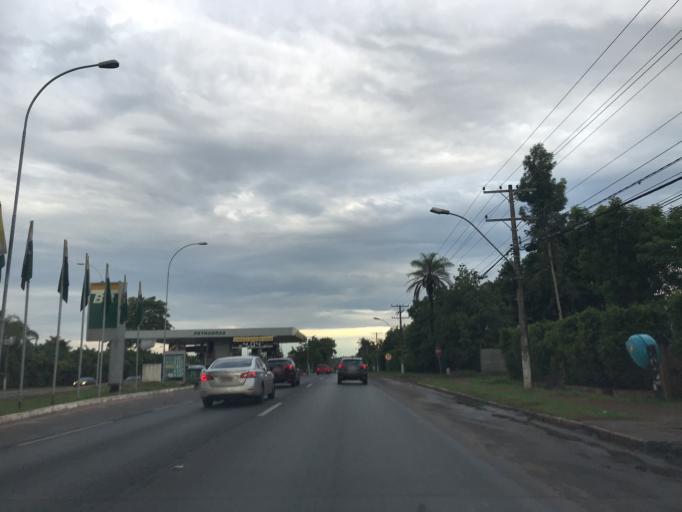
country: BR
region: Federal District
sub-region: Brasilia
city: Brasilia
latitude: -15.8580
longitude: -47.8645
